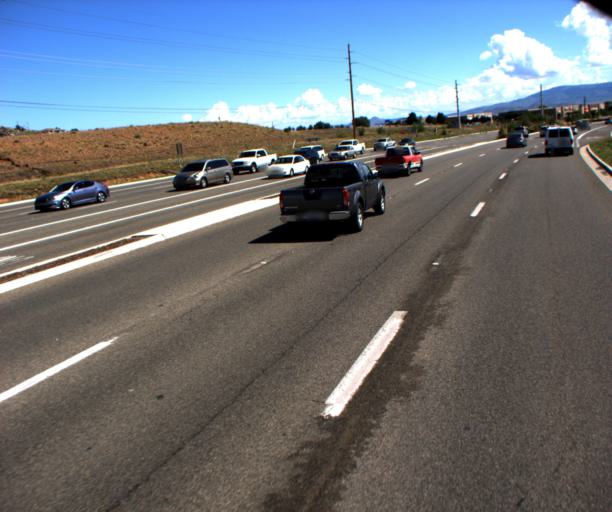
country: US
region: Arizona
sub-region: Yavapai County
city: Prescott Valley
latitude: 34.5770
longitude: -112.3647
